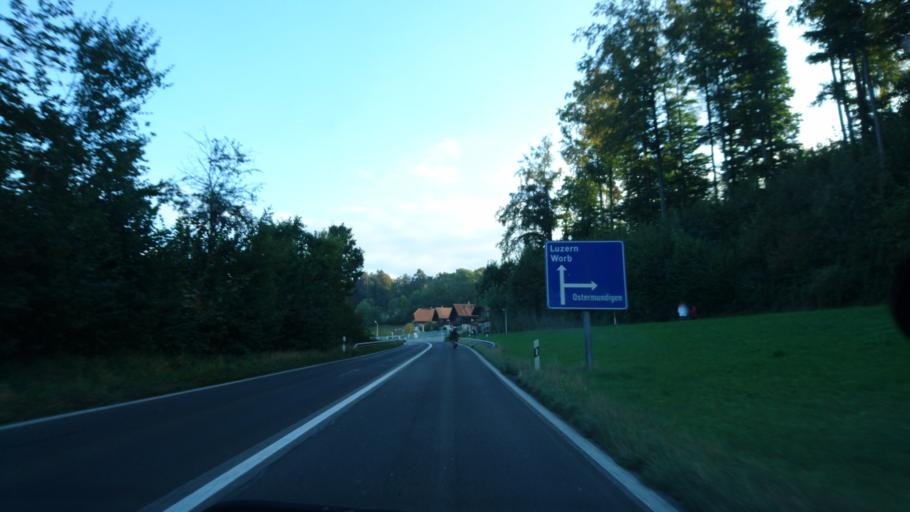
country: CH
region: Bern
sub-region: Bern-Mittelland District
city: Bolligen
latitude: 46.9625
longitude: 7.5049
